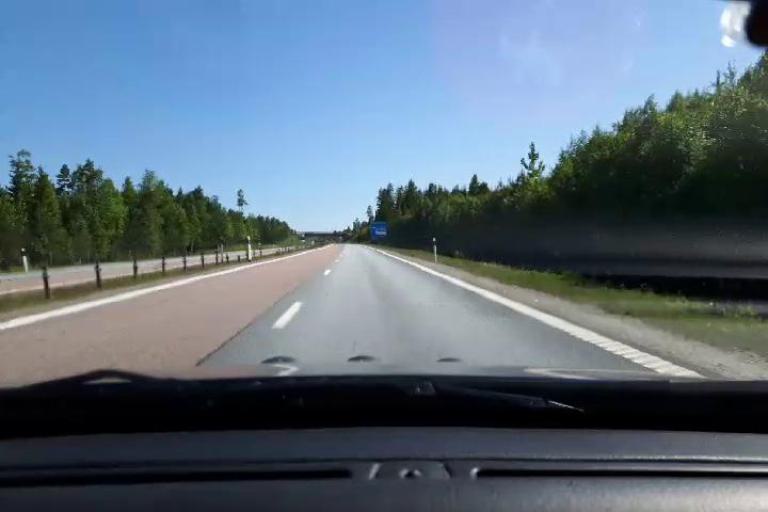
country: SE
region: Gaevleborg
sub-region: Hudiksvalls Kommun
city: Iggesund
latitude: 61.5249
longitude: 16.9737
